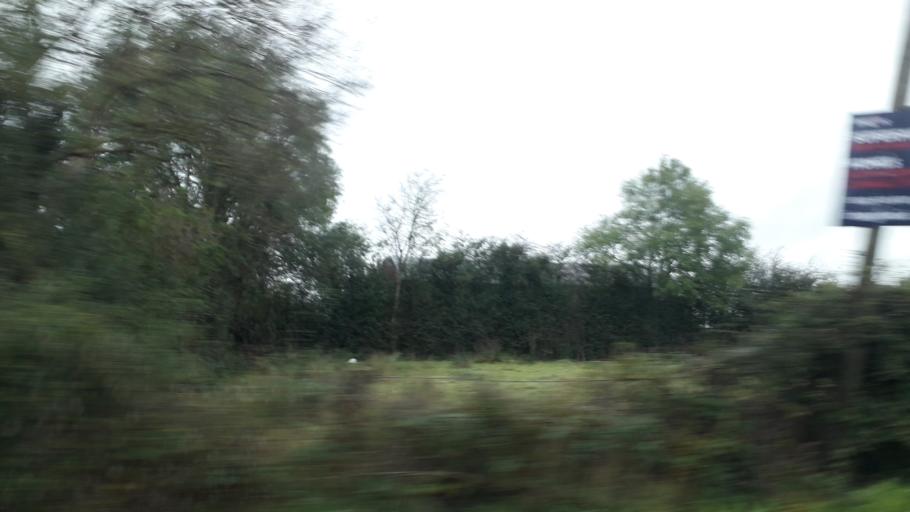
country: IE
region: Connaught
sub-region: Roscommon
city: Ballaghaderreen
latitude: 53.8924
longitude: -8.5541
